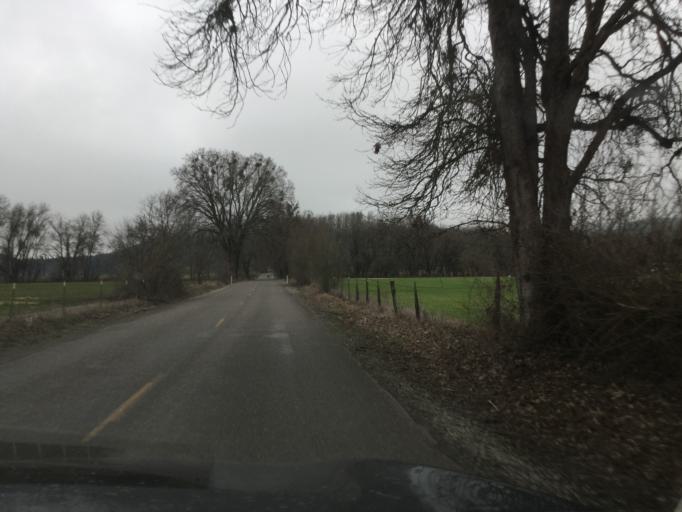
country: US
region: Oregon
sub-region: Jackson County
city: Central Point
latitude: 42.3967
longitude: -122.9686
